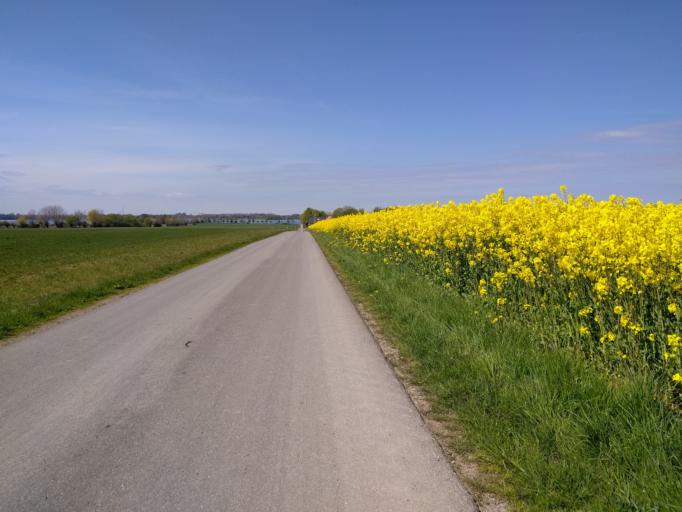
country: DK
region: South Denmark
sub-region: Kerteminde Kommune
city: Munkebo
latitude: 55.4453
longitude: 10.5938
